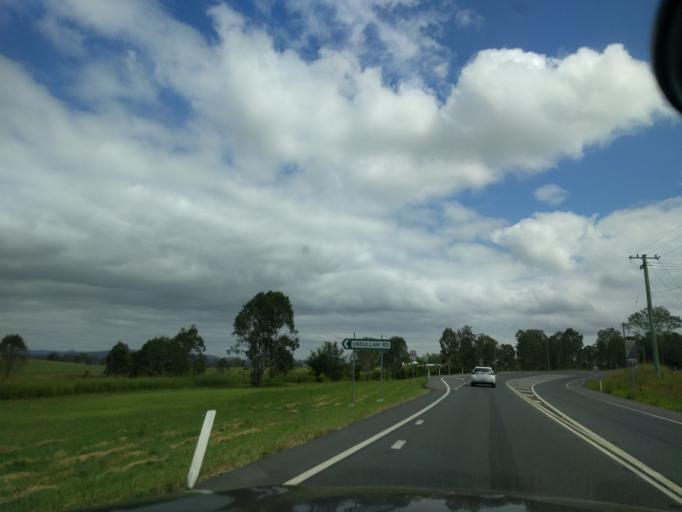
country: AU
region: Queensland
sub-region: Logan
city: Cedar Vale
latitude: -27.8925
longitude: 152.9735
